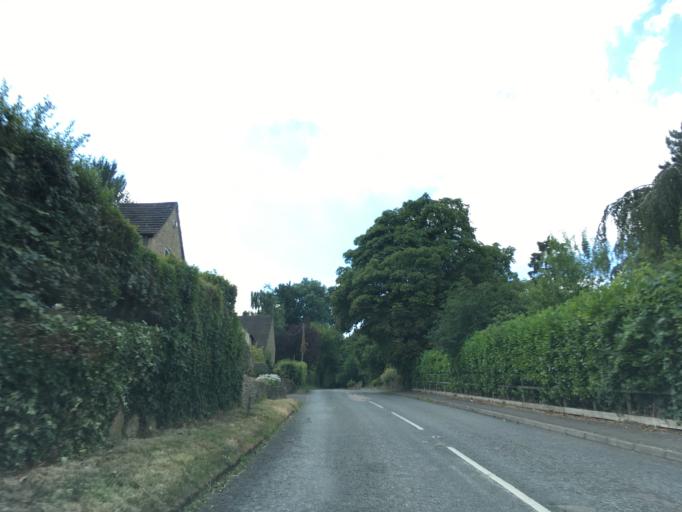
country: GB
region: England
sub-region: Gloucestershire
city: Barnwood
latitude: 51.8274
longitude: -2.2063
